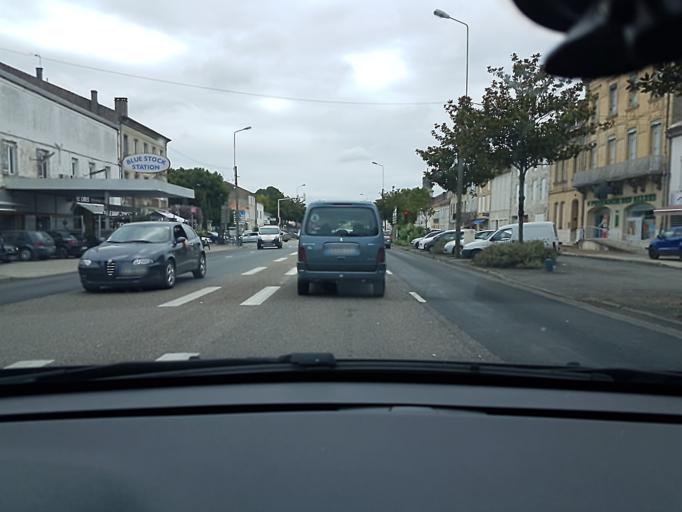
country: FR
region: Aquitaine
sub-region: Departement du Lot-et-Garonne
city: Nerac
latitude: 44.1350
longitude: 0.3370
